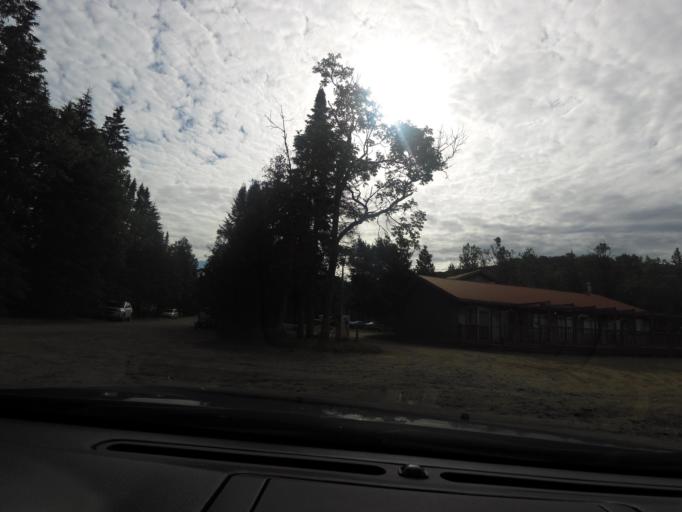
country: CA
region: Ontario
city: Huntsville
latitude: 45.6312
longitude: -79.1534
